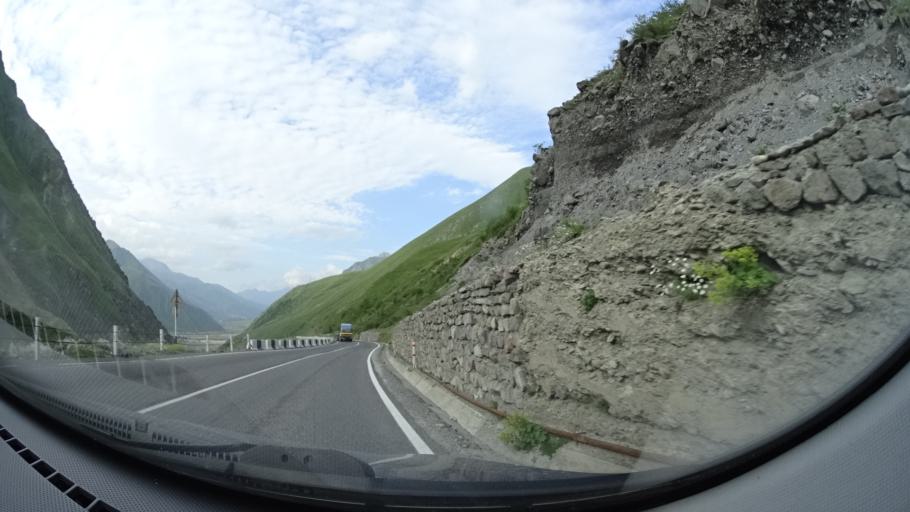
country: GE
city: Gudauri
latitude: 42.5395
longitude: 44.4861
